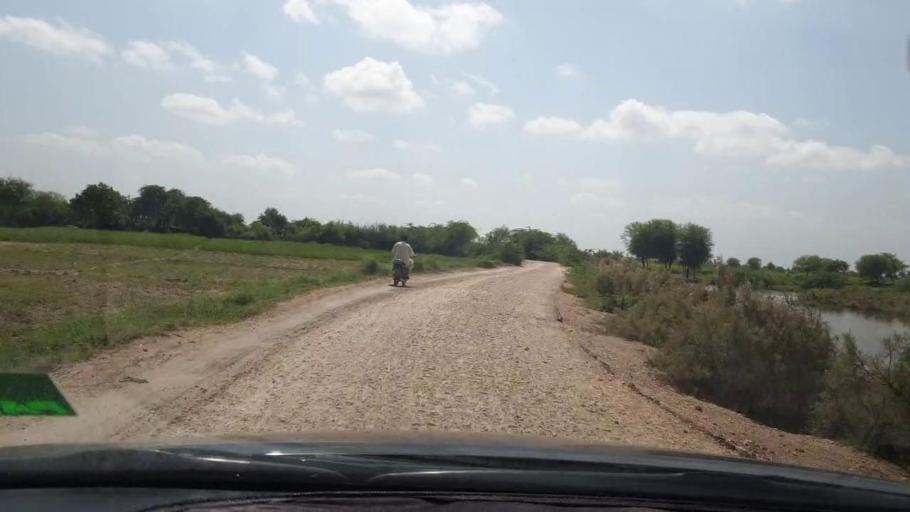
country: PK
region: Sindh
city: Tando Bago
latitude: 24.8804
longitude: 69.0801
